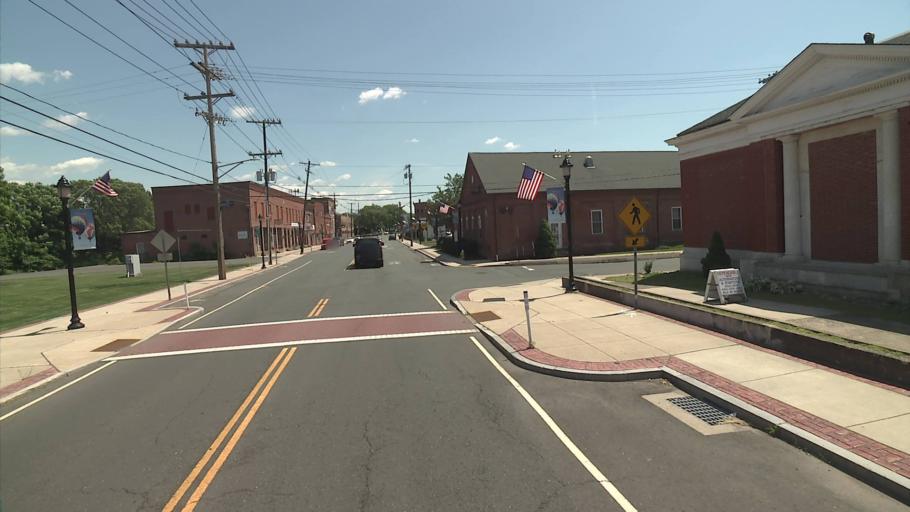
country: US
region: Connecticut
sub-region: Hartford County
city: Plainville
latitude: 41.6707
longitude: -72.8697
